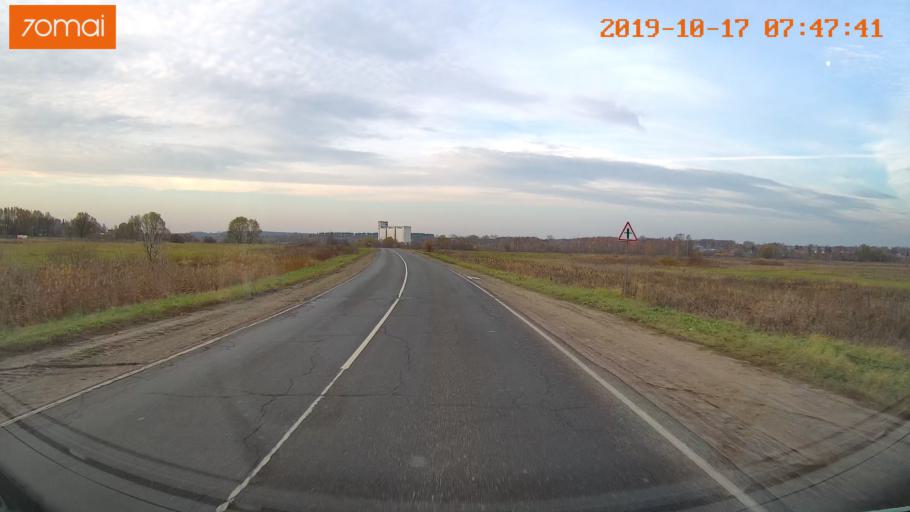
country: RU
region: Vladimir
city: Yur'yev-Pol'skiy
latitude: 56.4868
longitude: 39.6822
